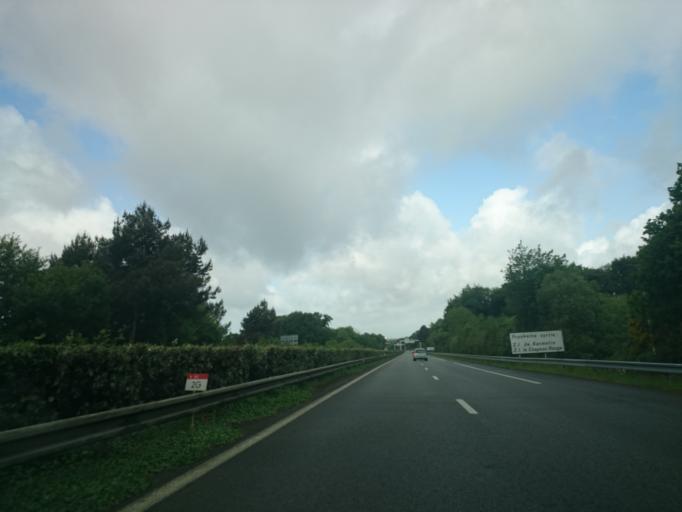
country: FR
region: Brittany
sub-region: Departement du Morbihan
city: Vannes
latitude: 47.6722
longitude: -2.7048
